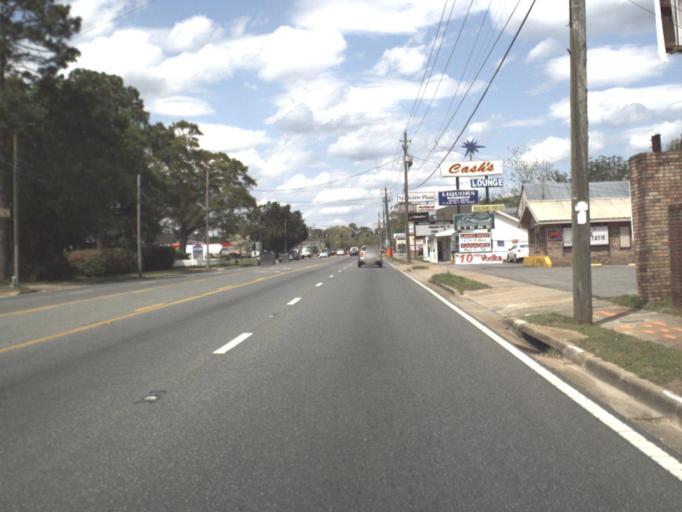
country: US
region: Florida
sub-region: Okaloosa County
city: Crestview
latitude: 30.7707
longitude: -86.5660
